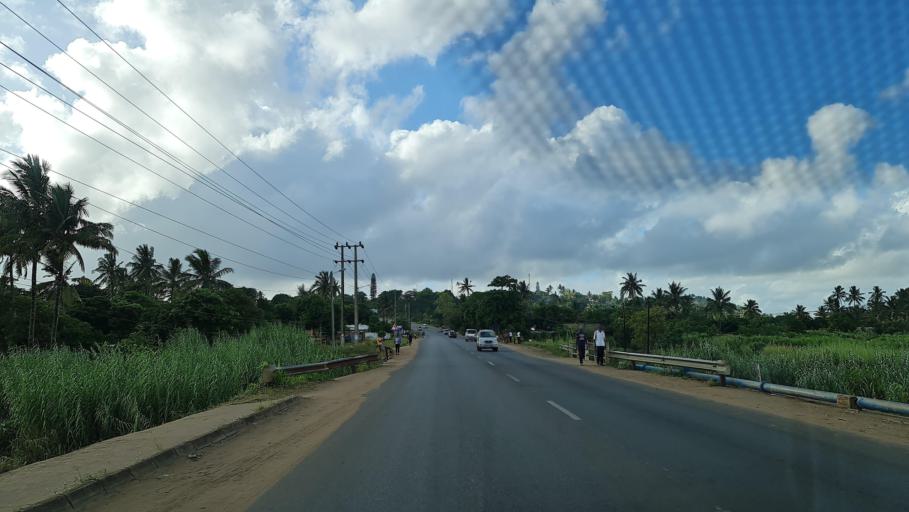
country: MZ
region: Gaza
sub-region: Xai-Xai District
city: Xai-Xai
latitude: -25.0530
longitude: 33.6488
